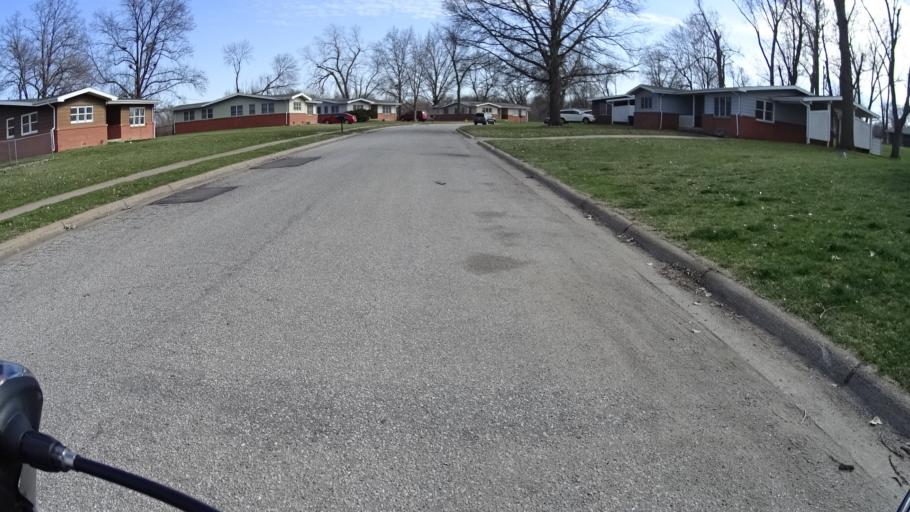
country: US
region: Nebraska
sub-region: Sarpy County
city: Offutt Air Force Base
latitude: 41.1197
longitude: -95.9586
